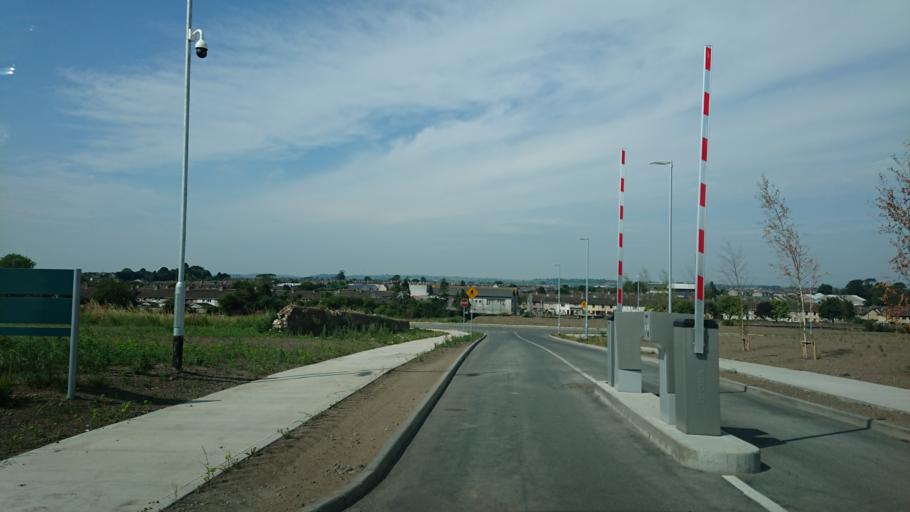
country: IE
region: Munster
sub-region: Waterford
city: Waterford
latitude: 52.2443
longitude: -7.1034
